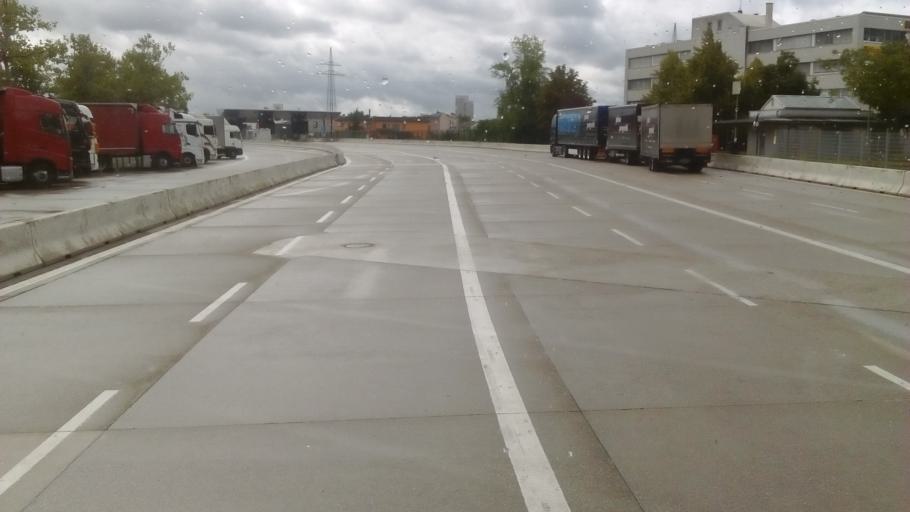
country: DE
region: Baden-Wuerttemberg
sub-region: Freiburg Region
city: Weil am Rhein
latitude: 47.6008
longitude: 7.6012
